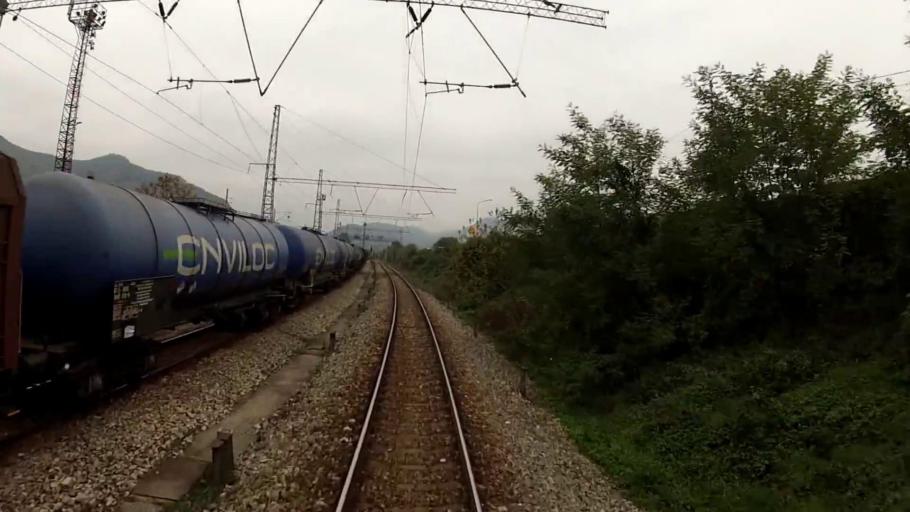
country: RS
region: Central Serbia
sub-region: Pirotski Okrug
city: Dimitrovgrad
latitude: 42.9913
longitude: 22.8508
